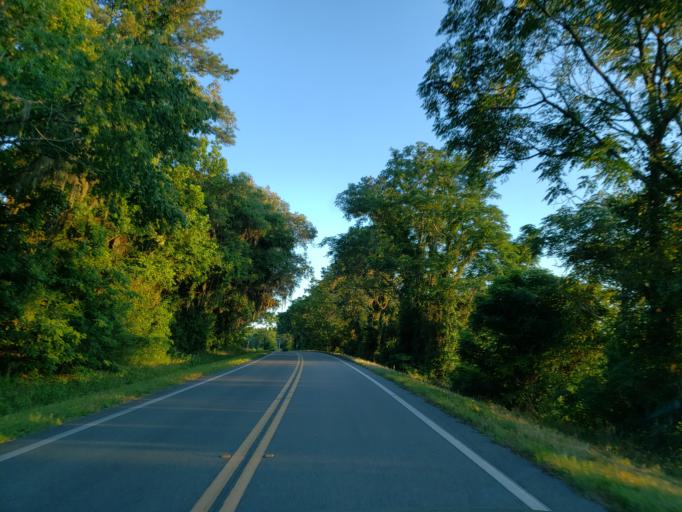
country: US
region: Florida
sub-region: Madison County
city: Madison
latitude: 30.6051
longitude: -83.2545
